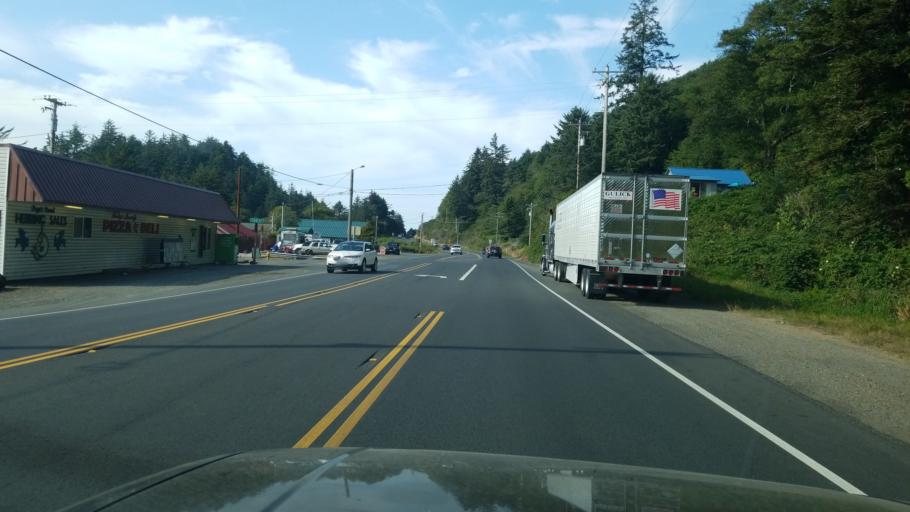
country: US
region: Oregon
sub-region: Tillamook County
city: Rockaway Beach
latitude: 45.5695
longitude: -123.9423
